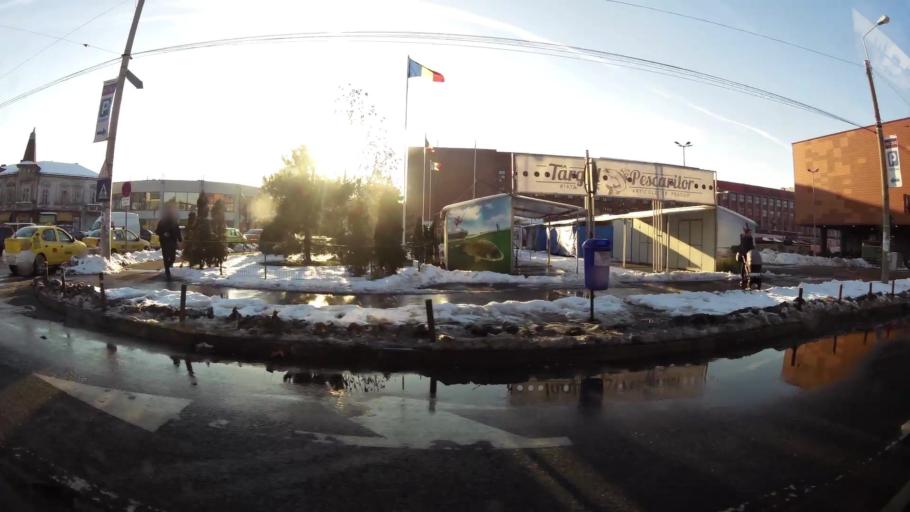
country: RO
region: Bucuresti
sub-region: Municipiul Bucuresti
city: Bucharest
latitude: 44.4492
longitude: 26.1311
